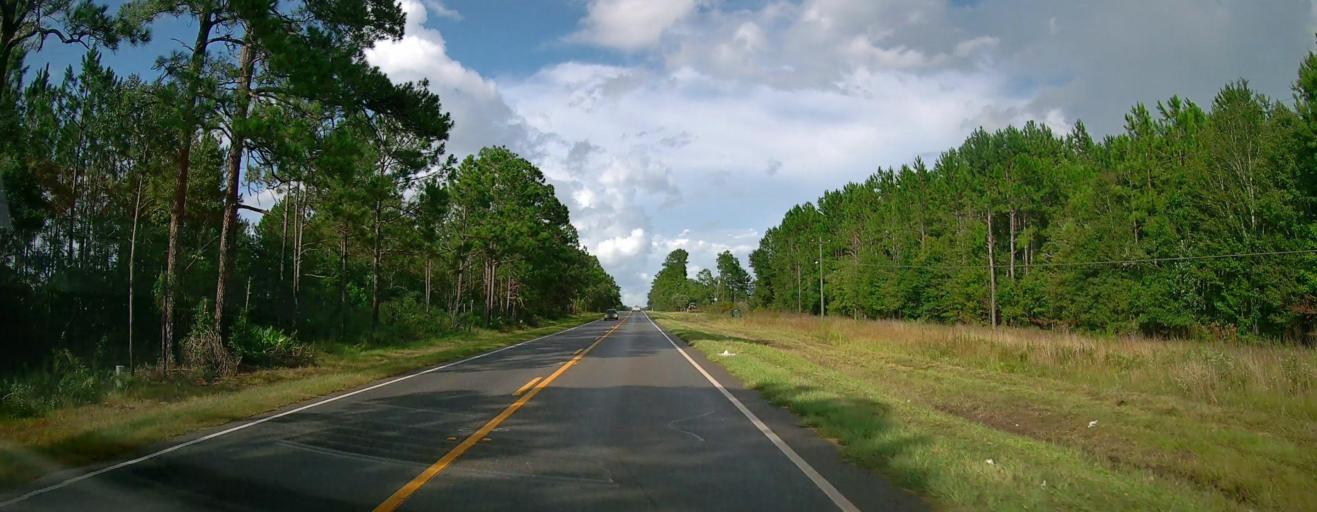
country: US
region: Georgia
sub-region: Coffee County
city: Douglas
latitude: 31.4739
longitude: -82.8745
